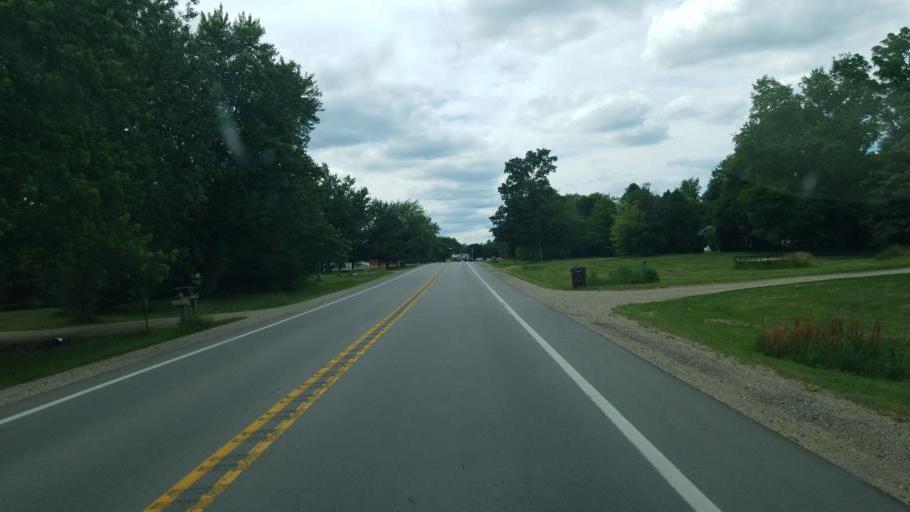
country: US
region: Michigan
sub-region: Eaton County
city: Charlotte
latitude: 42.6155
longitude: -84.8484
